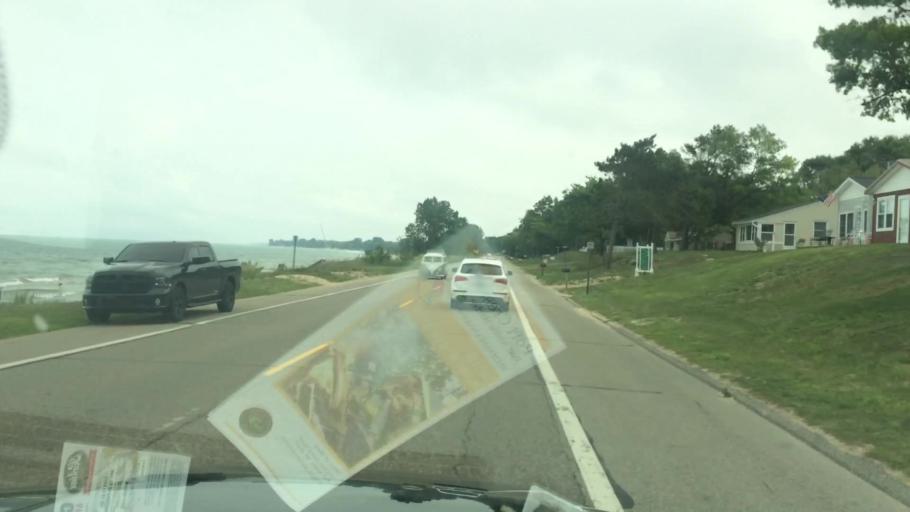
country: US
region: Michigan
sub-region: Huron County
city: Pigeon
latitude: 43.9871
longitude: -83.1524
